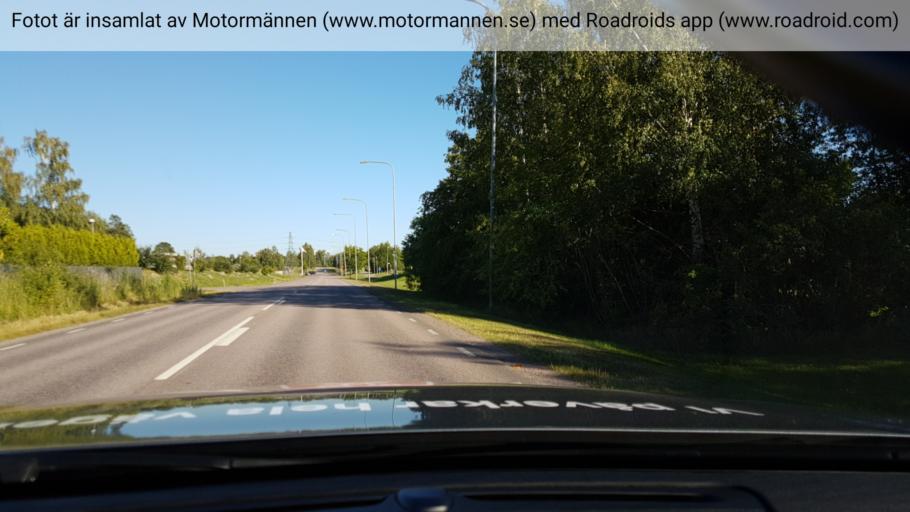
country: SE
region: Vaestmanland
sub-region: Vasteras
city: Vasteras
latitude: 59.6302
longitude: 16.4985
